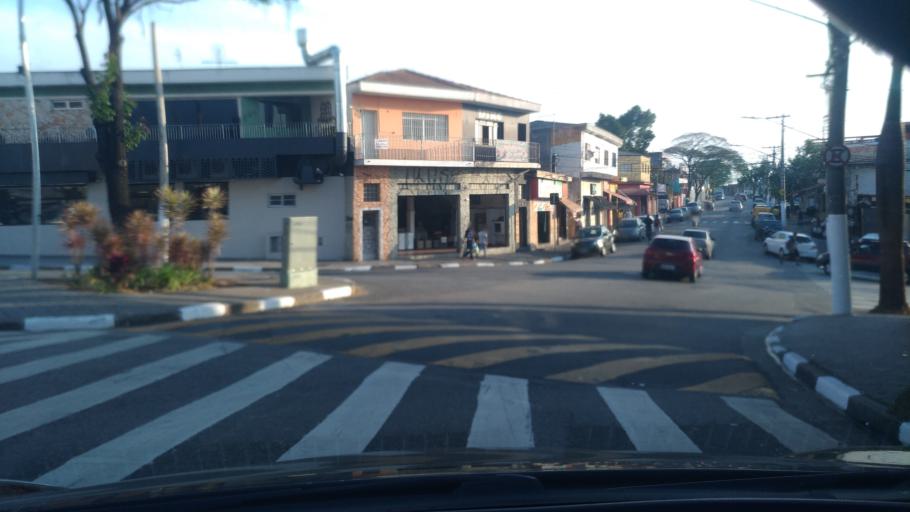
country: BR
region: Sao Paulo
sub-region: Osasco
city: Osasco
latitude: -23.5407
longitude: -46.7949
